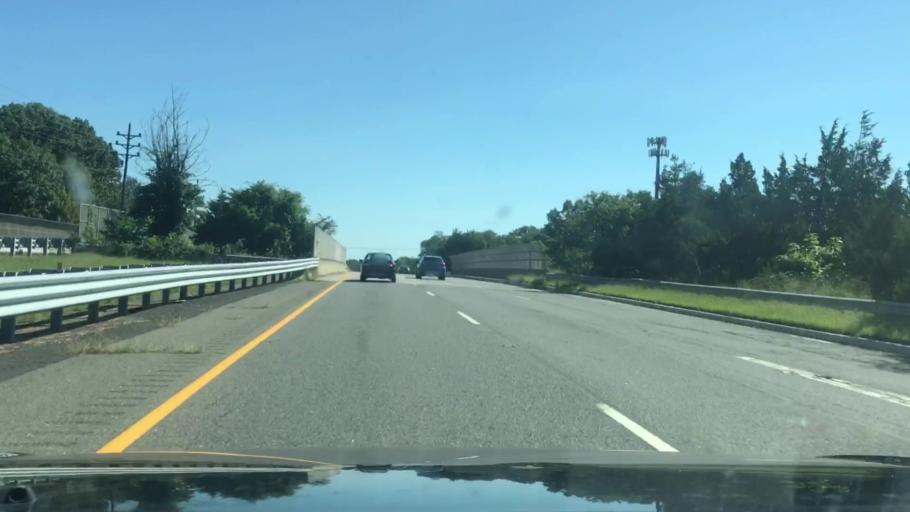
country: US
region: New Jersey
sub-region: Monmouth County
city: Shark River Hills
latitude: 40.1711
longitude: -74.0726
